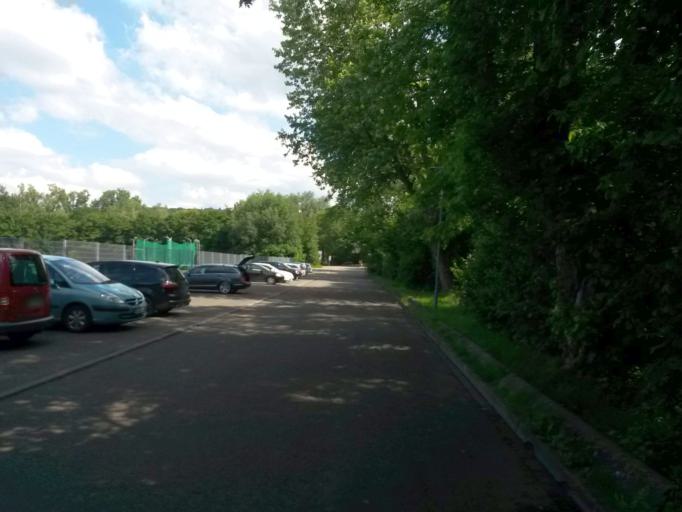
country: DE
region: Baden-Wuerttemberg
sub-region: Karlsruhe Region
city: Konigsbach-Stein
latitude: 48.9433
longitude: 8.5730
